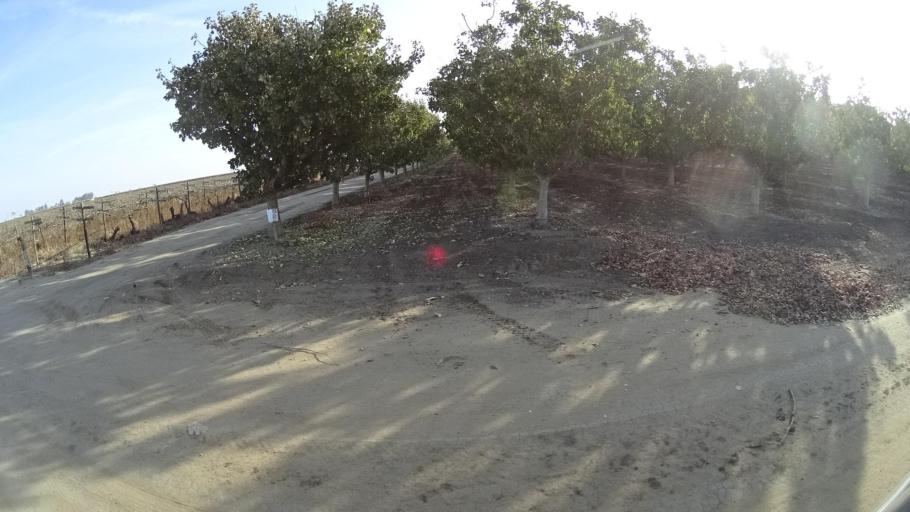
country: US
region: California
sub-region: Kern County
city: McFarland
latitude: 35.7323
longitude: -119.1873
